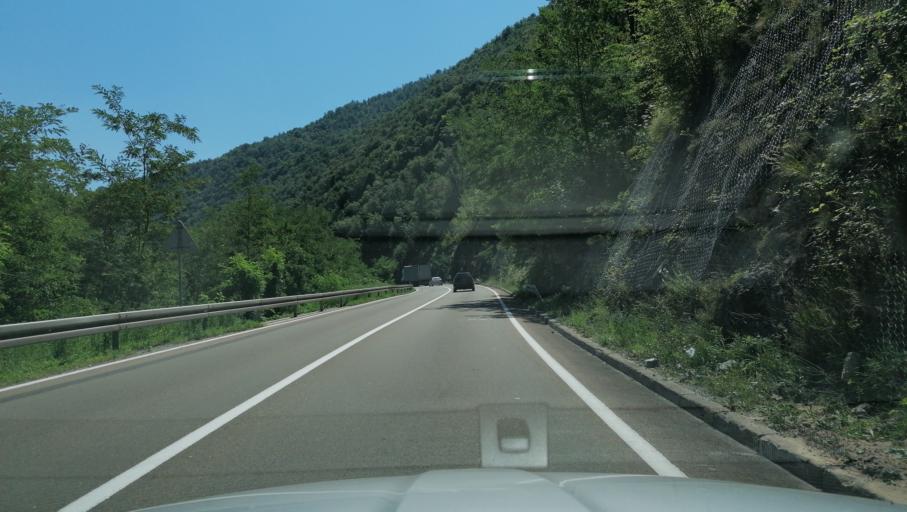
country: RS
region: Central Serbia
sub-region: Raski Okrug
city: Kraljevo
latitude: 43.5659
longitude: 20.6025
